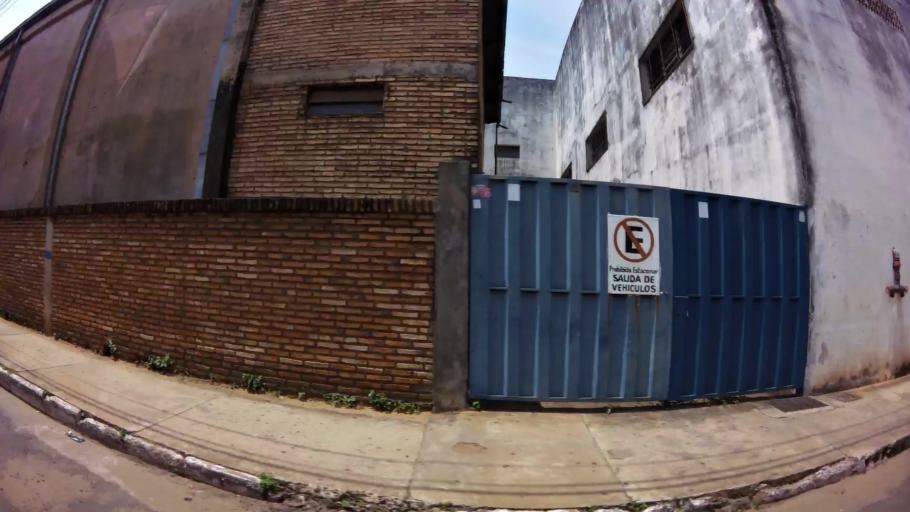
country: PY
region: Central
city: Fernando de la Mora
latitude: -25.3201
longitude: -57.5581
